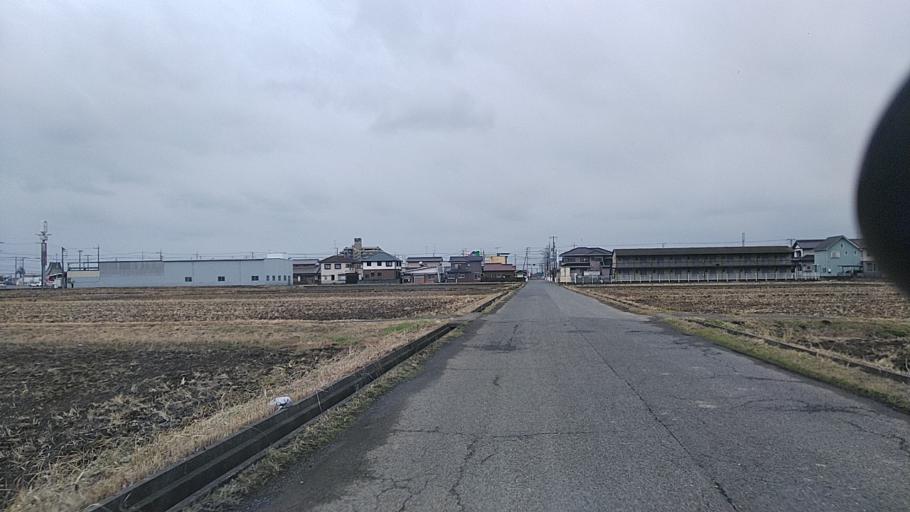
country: JP
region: Chiba
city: Togane
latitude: 35.5781
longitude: 140.3786
